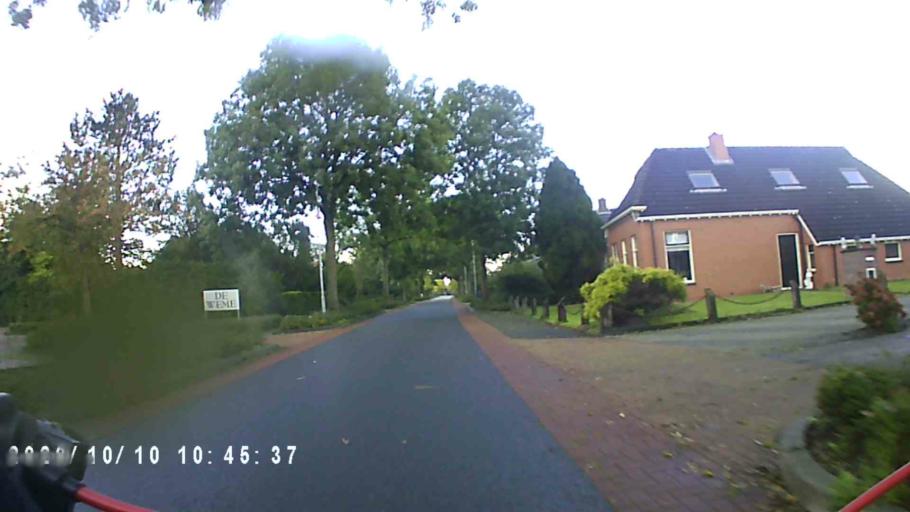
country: NL
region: Groningen
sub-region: Gemeente Grootegast
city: Grootegast
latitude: 53.1700
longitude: 6.2565
